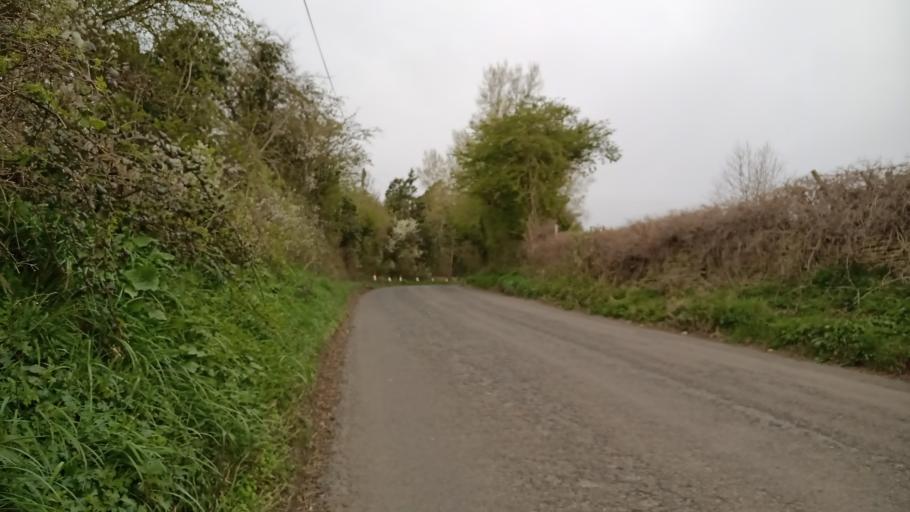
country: GB
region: England
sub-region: Oxfordshire
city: Witney
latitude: 51.7986
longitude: -1.4964
